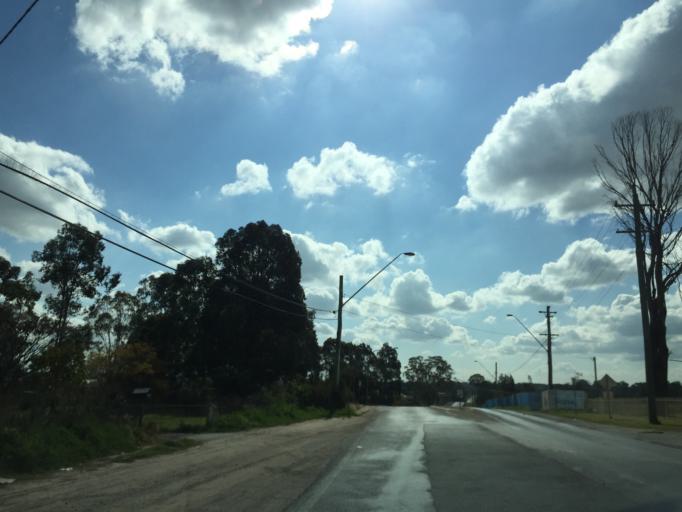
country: AU
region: New South Wales
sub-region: Blacktown
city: Quakers Hill
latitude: -33.7070
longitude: 150.8938
